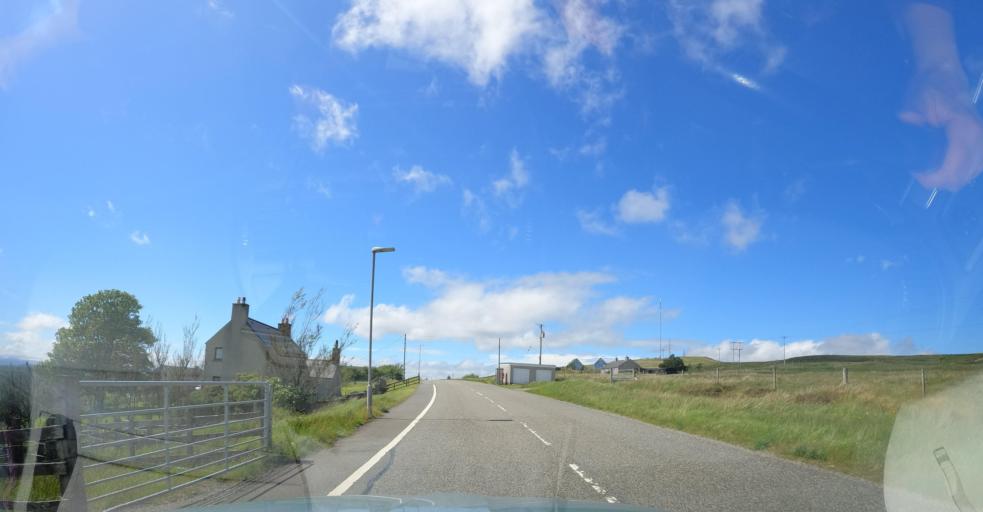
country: GB
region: Scotland
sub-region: Eilean Siar
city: Stornoway
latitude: 58.1712
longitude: -6.5707
